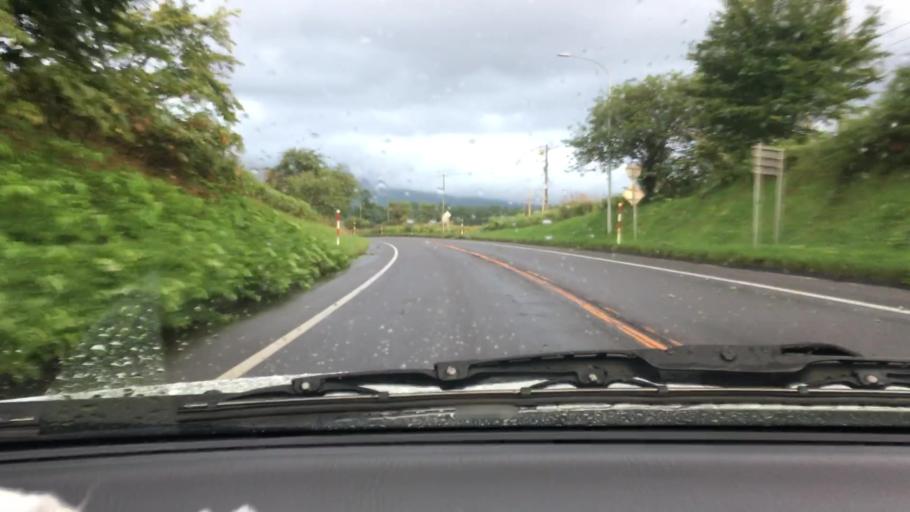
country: JP
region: Hokkaido
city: Nanae
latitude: 42.0812
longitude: 140.5898
